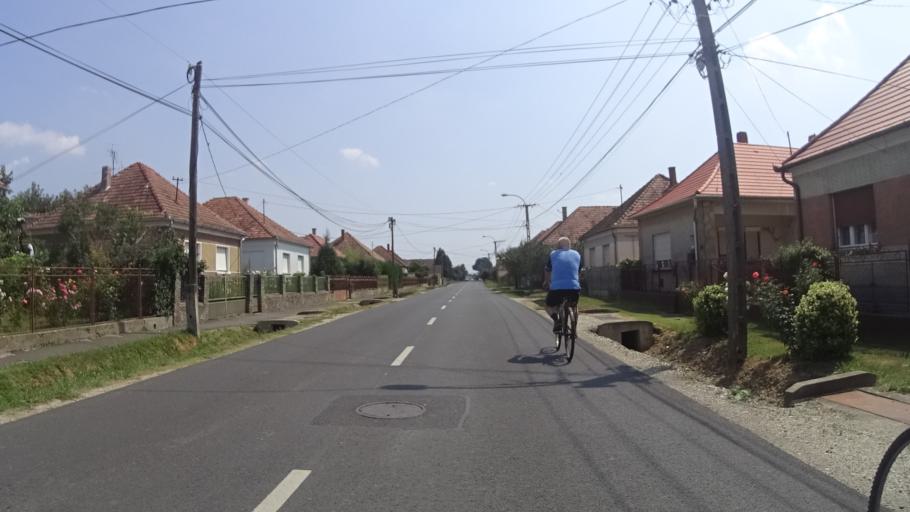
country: HU
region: Zala
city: Letenye
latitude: 46.4250
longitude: 16.7294
